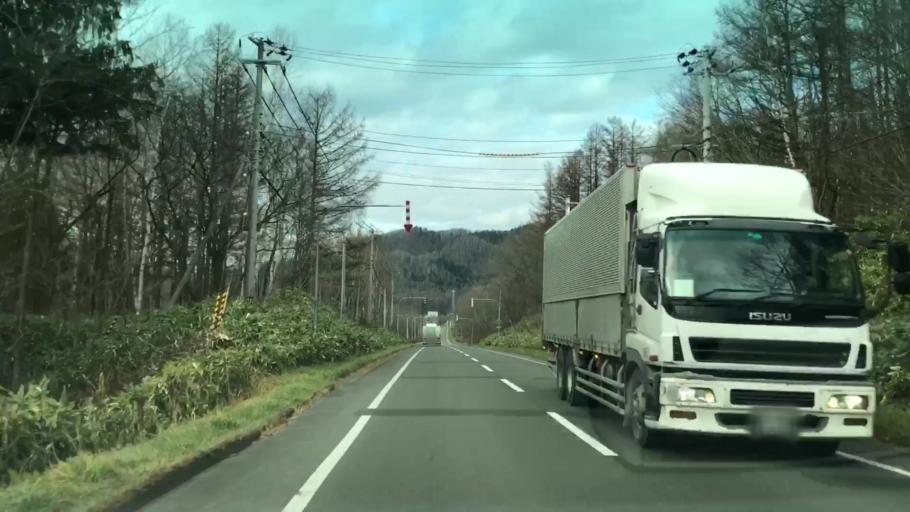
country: JP
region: Hokkaido
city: Shimo-furano
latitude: 42.9414
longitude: 142.4443
